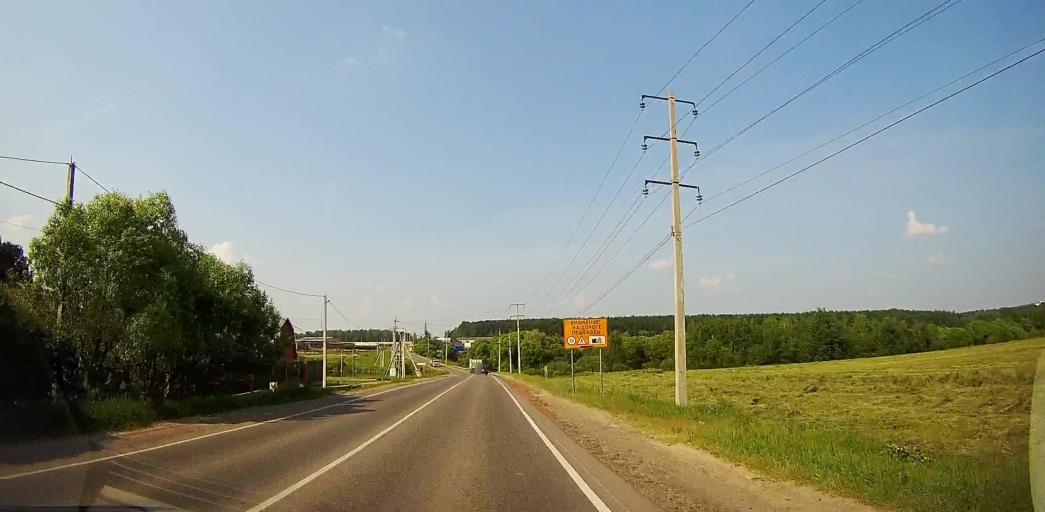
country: RU
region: Moskovskaya
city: Barybino
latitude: 55.2736
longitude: 37.9159
